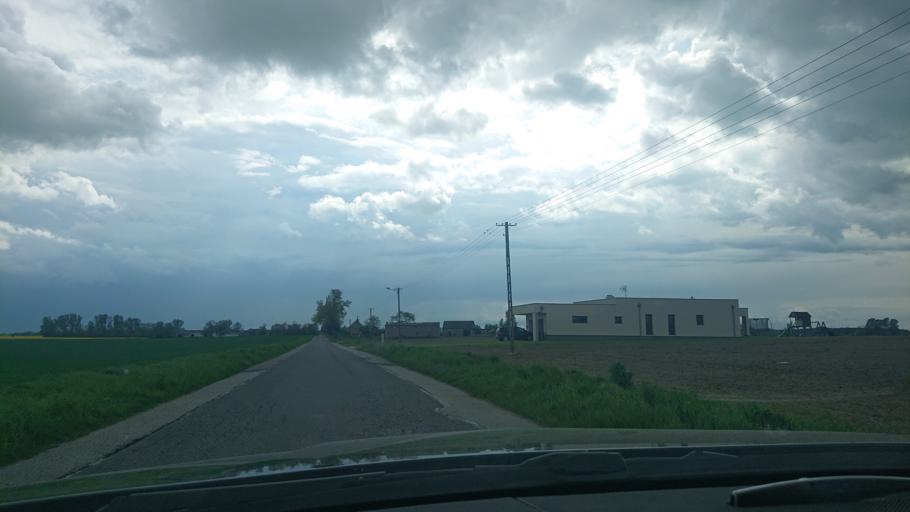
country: PL
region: Greater Poland Voivodeship
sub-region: Powiat gnieznienski
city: Niechanowo
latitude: 52.4765
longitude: 17.6388
